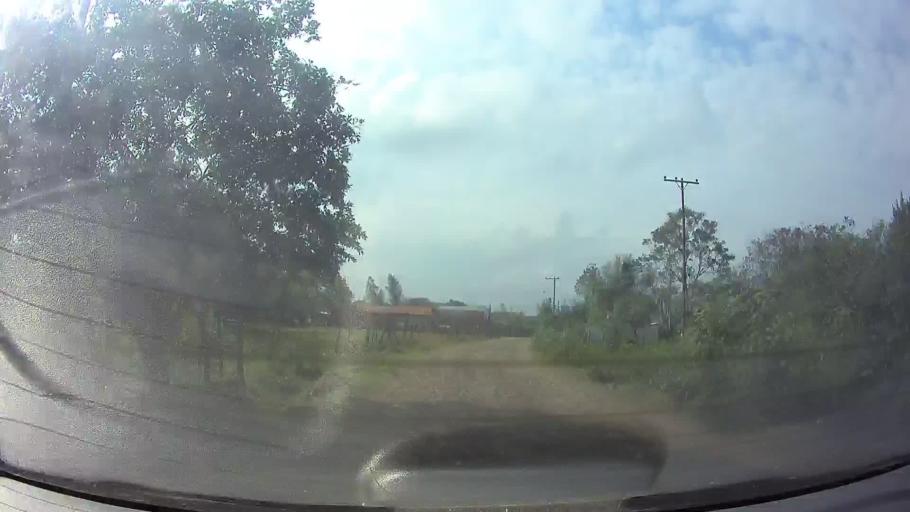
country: PY
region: Cordillera
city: Arroyos y Esteros
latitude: -24.9970
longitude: -57.1944
